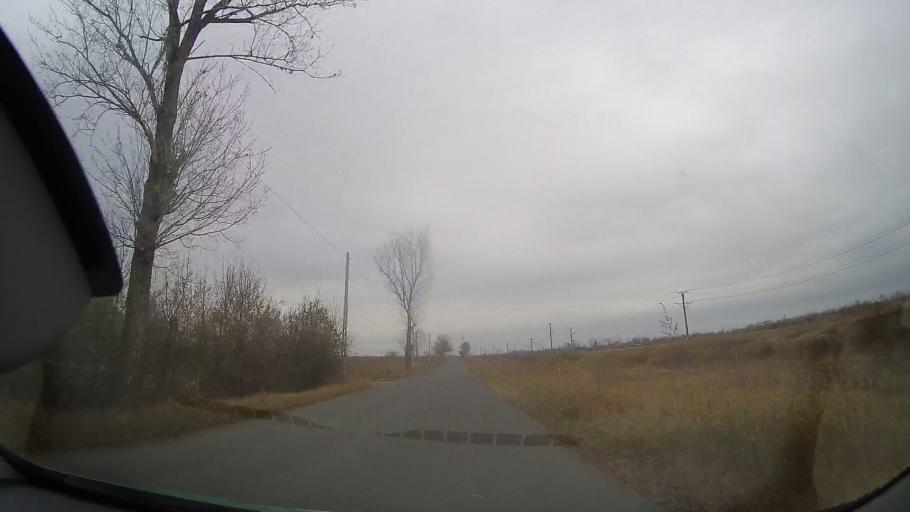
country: RO
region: Braila
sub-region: Comuna Rosiori
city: Rosiori
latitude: 44.8355
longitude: 27.3276
